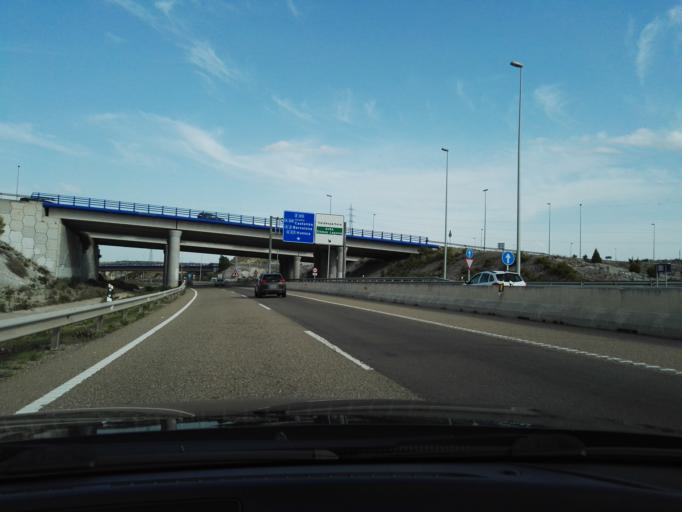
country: ES
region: Aragon
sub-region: Provincia de Zaragoza
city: Montecanal
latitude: 41.6144
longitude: -0.9334
